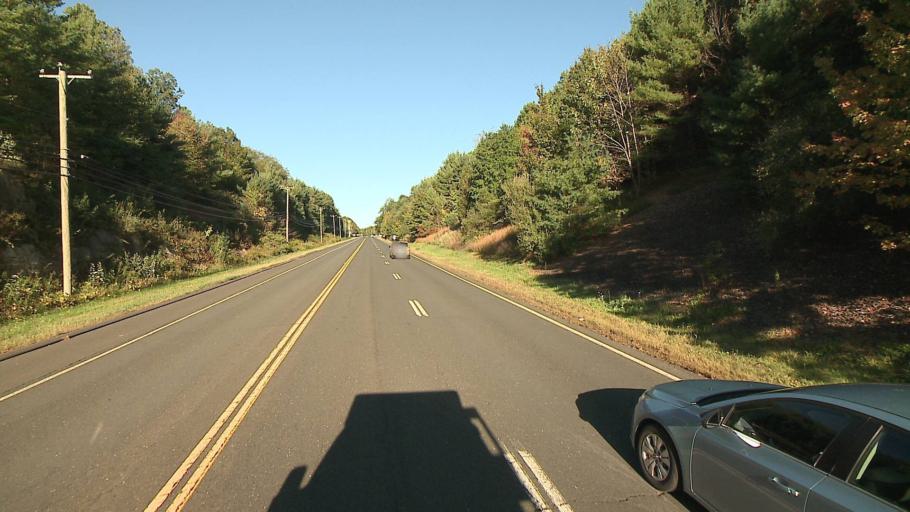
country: US
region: Connecticut
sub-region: Litchfield County
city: New Hartford Center
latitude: 41.8291
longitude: -73.0124
